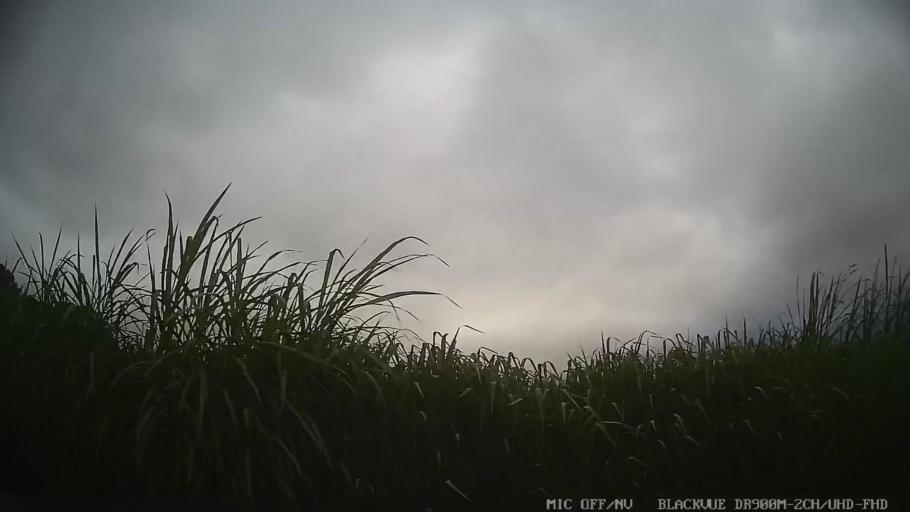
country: BR
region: Sao Paulo
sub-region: Biritiba-Mirim
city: Biritiba Mirim
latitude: -23.5629
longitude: -46.0858
